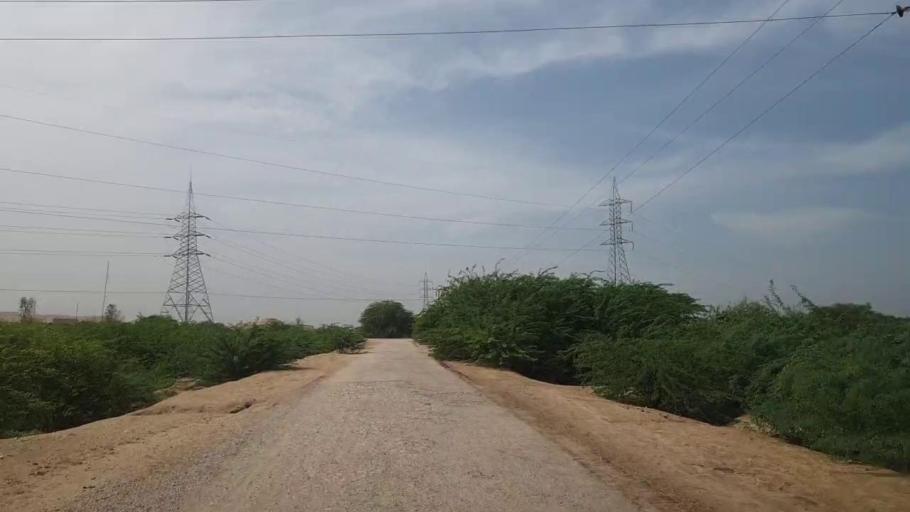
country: PK
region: Sindh
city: Kot Diji
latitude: 27.3625
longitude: 68.7632
